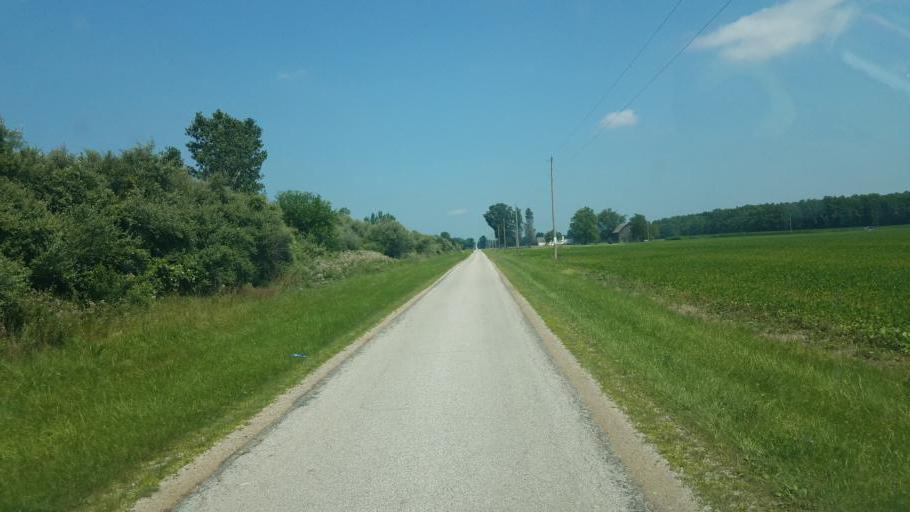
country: US
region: Ohio
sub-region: Sandusky County
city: Green Springs
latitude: 41.0633
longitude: -82.9770
